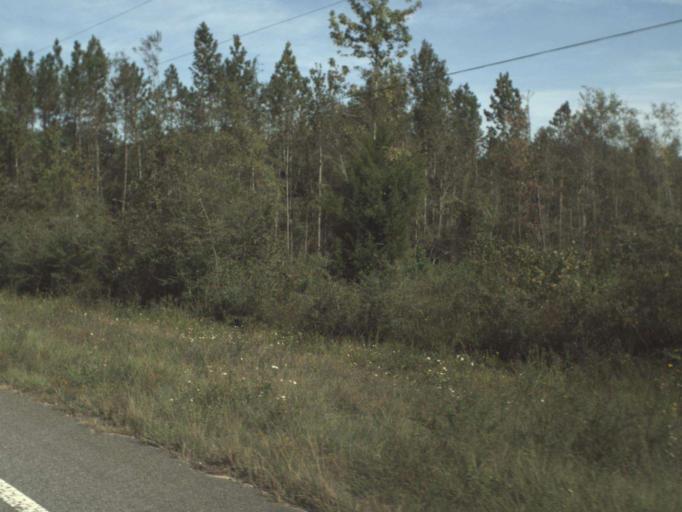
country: US
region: Florida
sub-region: Washington County
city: Chipley
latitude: 30.6127
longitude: -85.5944
